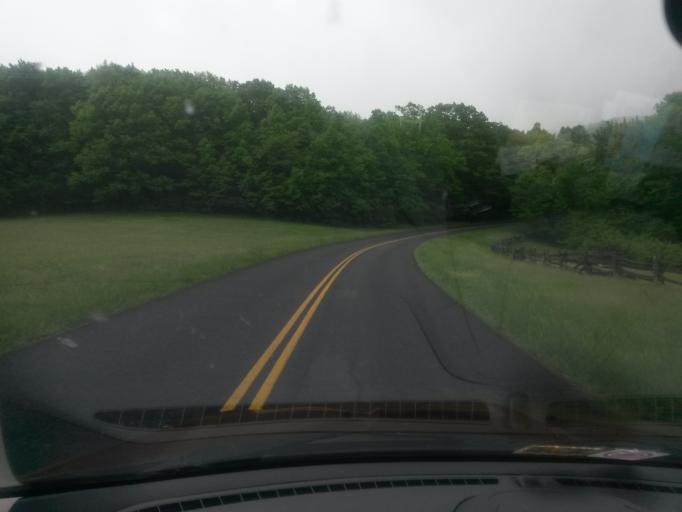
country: US
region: Virginia
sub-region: Floyd County
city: Floyd
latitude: 36.8318
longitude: -80.3283
